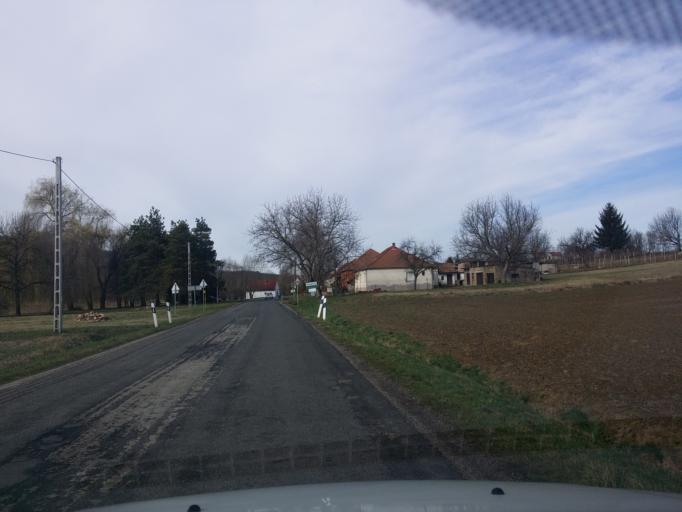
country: HU
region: Baranya
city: Villany
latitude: 45.8803
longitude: 18.4336
